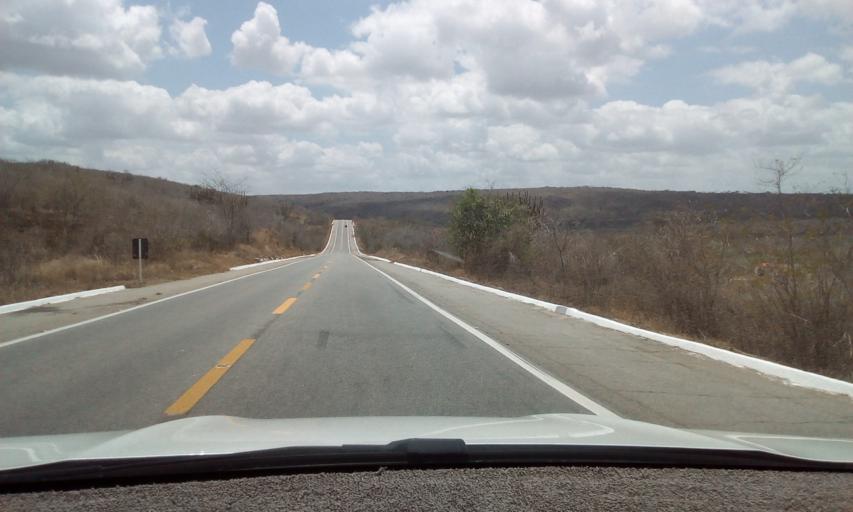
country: BR
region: Paraiba
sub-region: Boqueirao
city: Boqueirao
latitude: -7.6773
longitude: -36.0693
